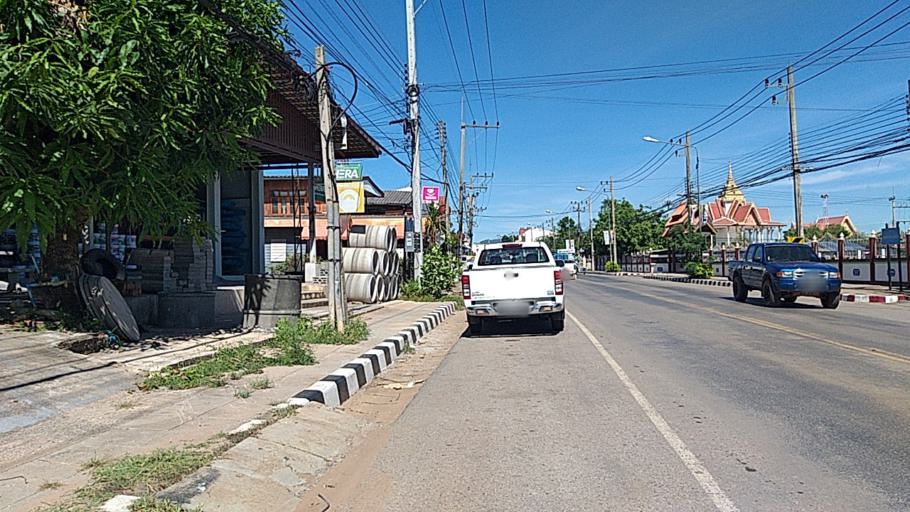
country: TH
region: Chaiyaphum
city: Ban Thaen
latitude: 16.4092
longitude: 102.3543
